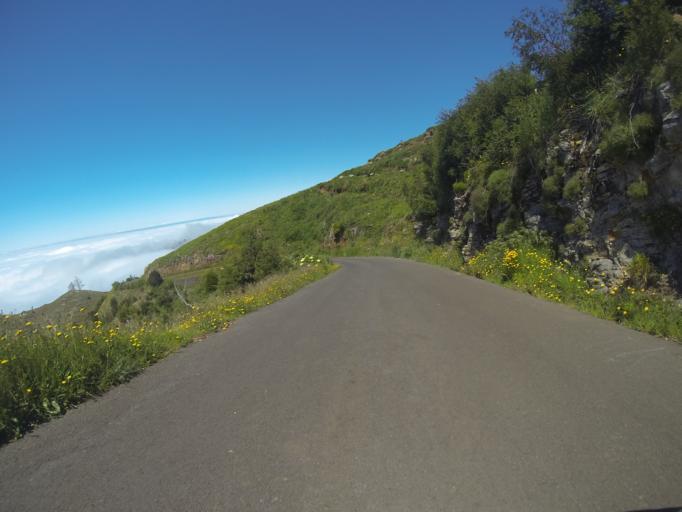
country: PT
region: Madeira
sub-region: Funchal
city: Nossa Senhora do Monte
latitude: 32.7034
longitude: -16.9129
